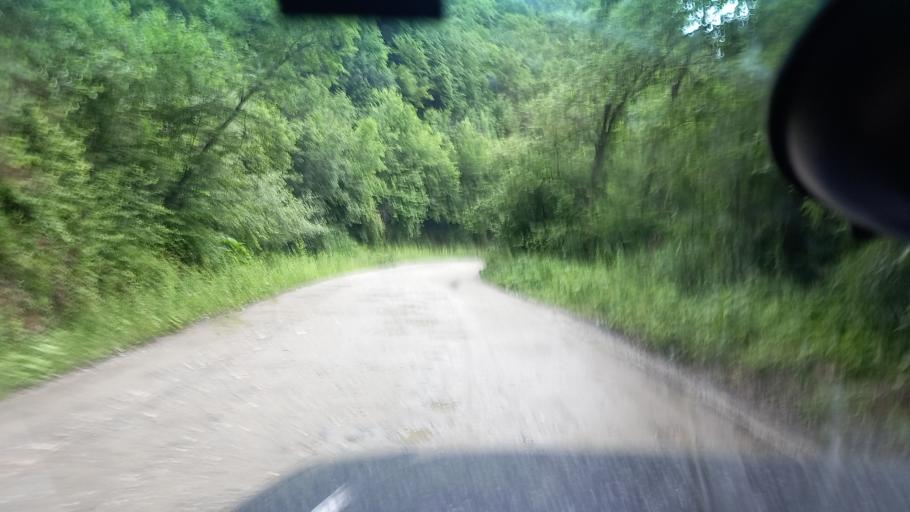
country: RU
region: Krasnodarskiy
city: Psebay
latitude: 44.0374
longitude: 40.7522
